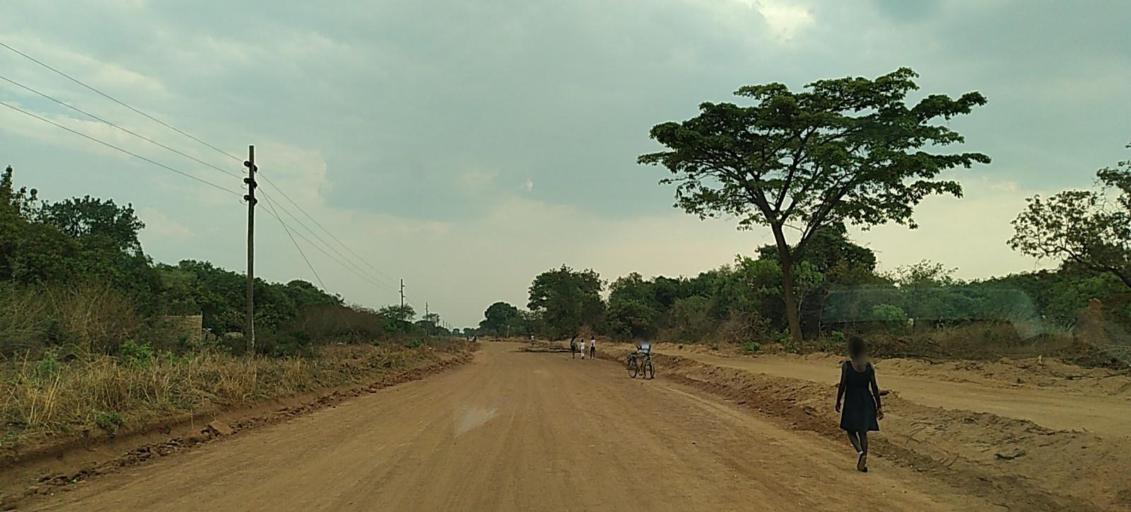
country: ZM
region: Copperbelt
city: Kalulushi
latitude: -12.9021
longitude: 27.9481
